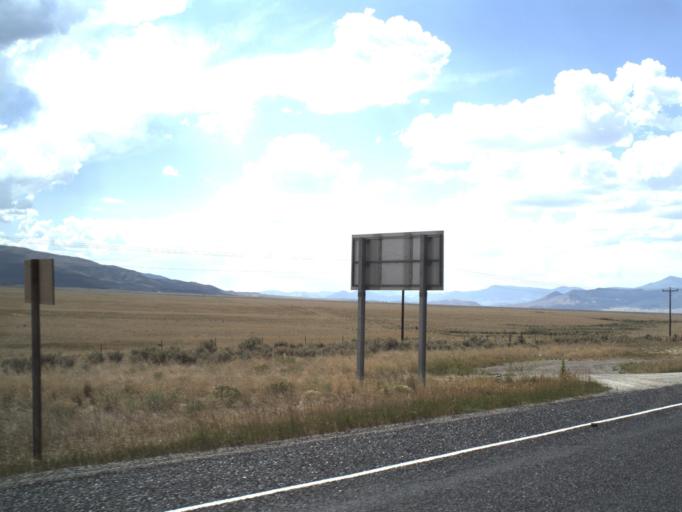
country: US
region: Idaho
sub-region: Minidoka County
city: Rupert
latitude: 41.9939
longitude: -113.1886
